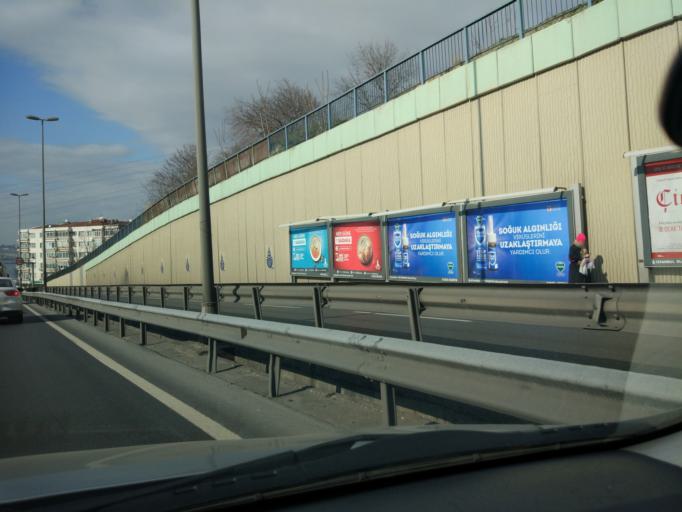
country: TR
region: Istanbul
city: Mahmutbey
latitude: 40.9860
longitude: 28.7777
